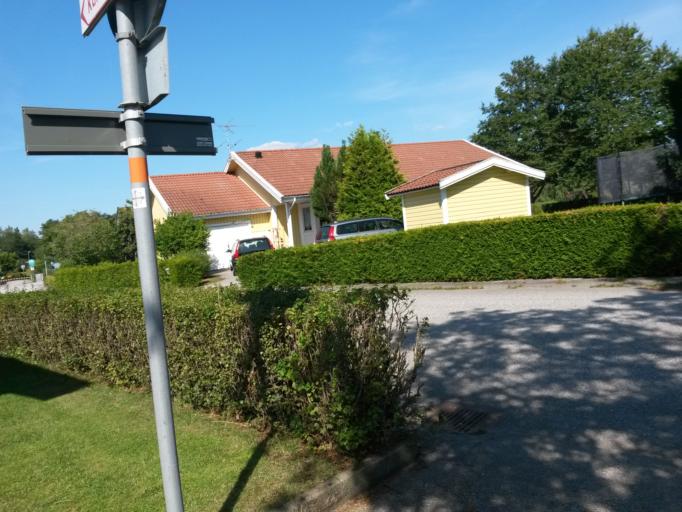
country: SE
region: Vaestra Goetaland
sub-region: Gotene Kommun
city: Kallby
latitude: 58.5058
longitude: 13.2987
